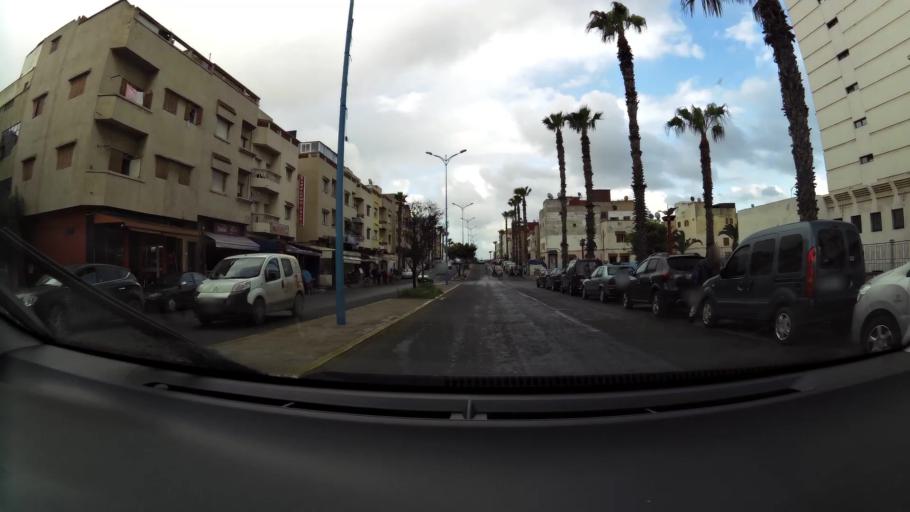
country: MA
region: Grand Casablanca
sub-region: Mohammedia
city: Mohammedia
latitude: 33.6857
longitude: -7.3888
